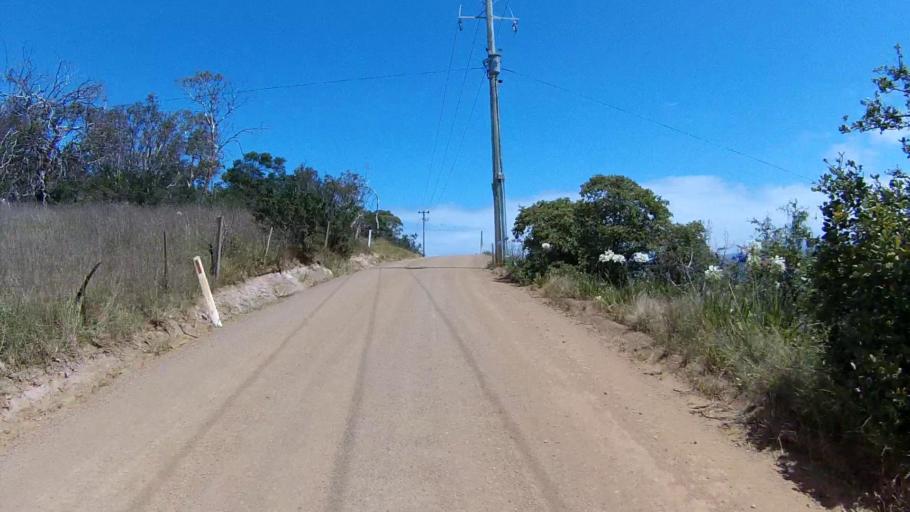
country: AU
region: Tasmania
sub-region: Clarence
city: Lauderdale
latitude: -42.9325
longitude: 147.4668
